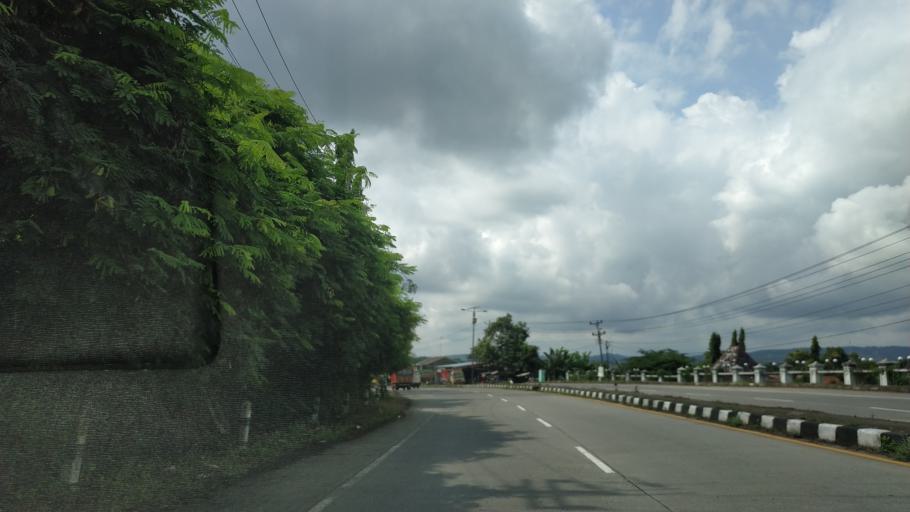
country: ID
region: Central Java
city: Pekalongan
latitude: -6.9501
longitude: 109.8270
